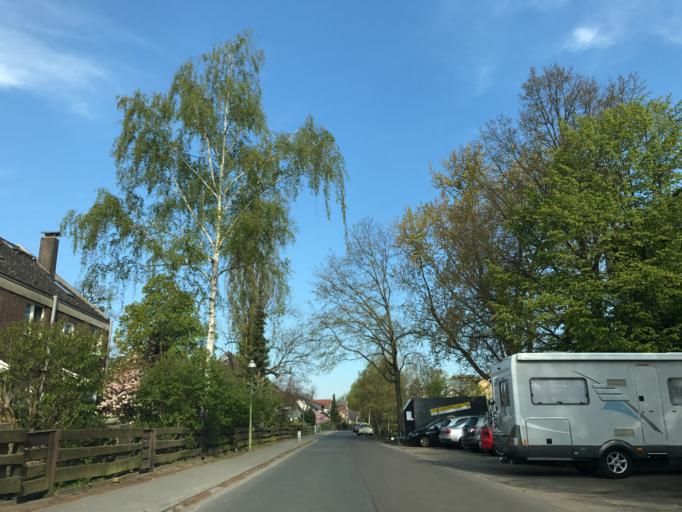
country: DE
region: Berlin
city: Wilhelmstadt
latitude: 52.5134
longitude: 13.1656
